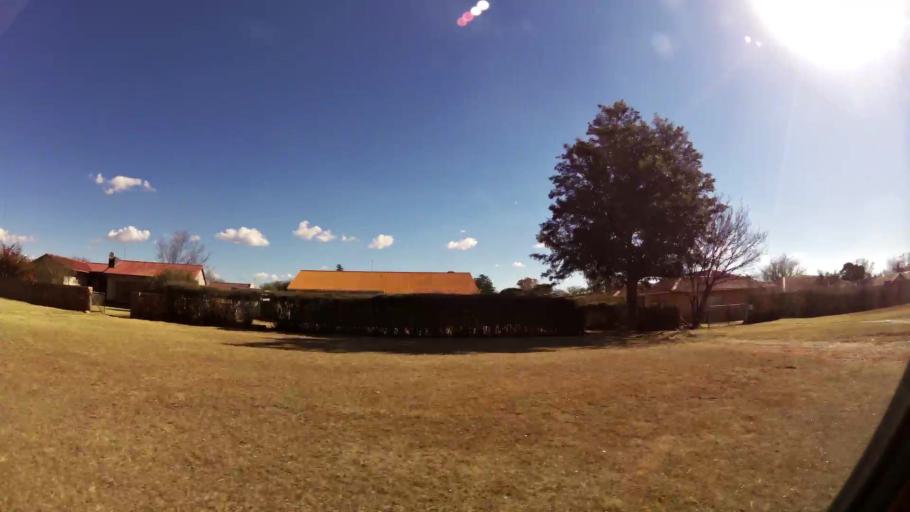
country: ZA
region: Gauteng
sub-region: West Rand District Municipality
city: Carletonville
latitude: -26.3717
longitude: 27.3852
